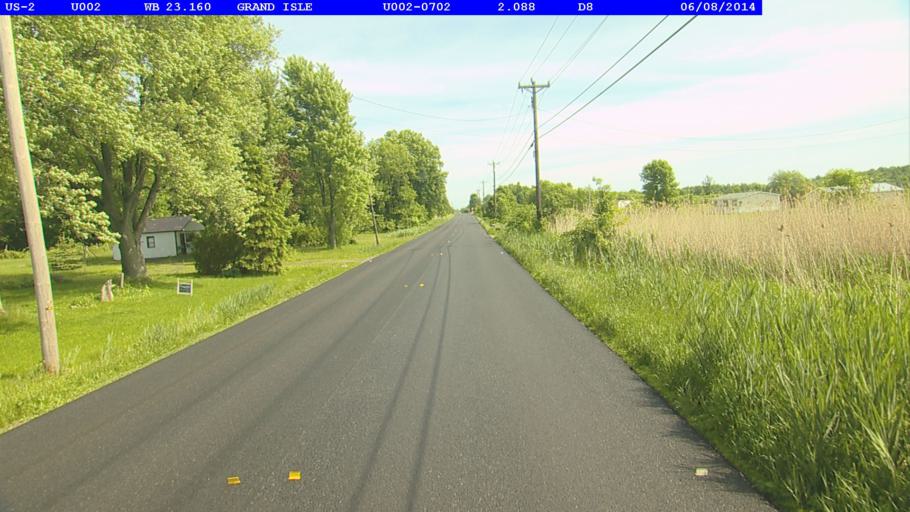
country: US
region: Vermont
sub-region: Grand Isle County
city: North Hero
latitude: 44.7373
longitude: -73.2902
